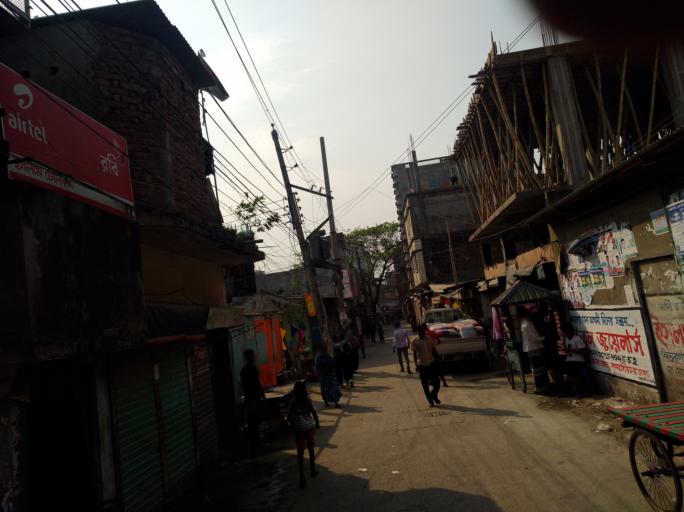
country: BD
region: Dhaka
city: Azimpur
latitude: 23.7147
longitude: 90.3748
